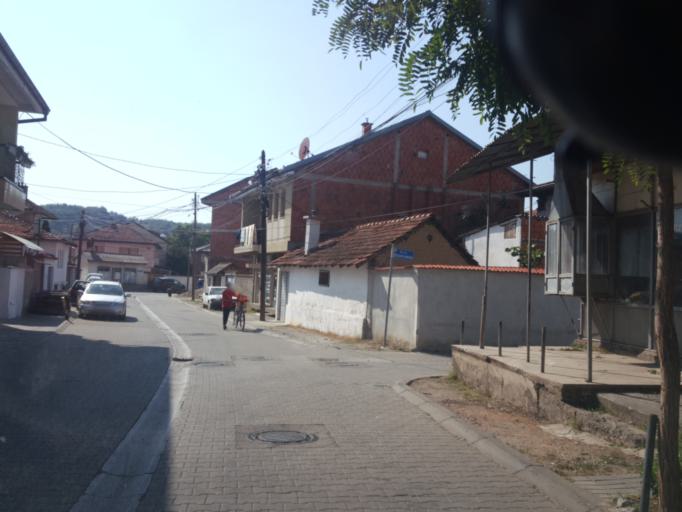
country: XK
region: Gjakova
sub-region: Komuna e Gjakoves
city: Gjakove
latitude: 42.3881
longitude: 20.4272
